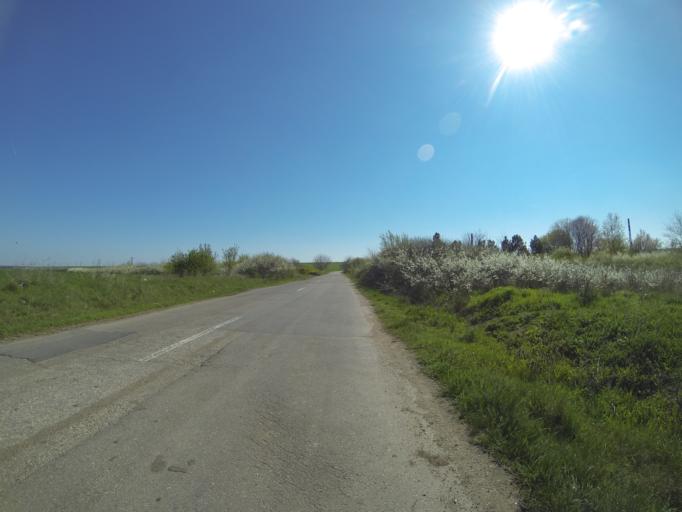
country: RO
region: Dolj
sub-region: Comuna Intorsura
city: Intorsura
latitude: 44.1344
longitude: 23.5937
